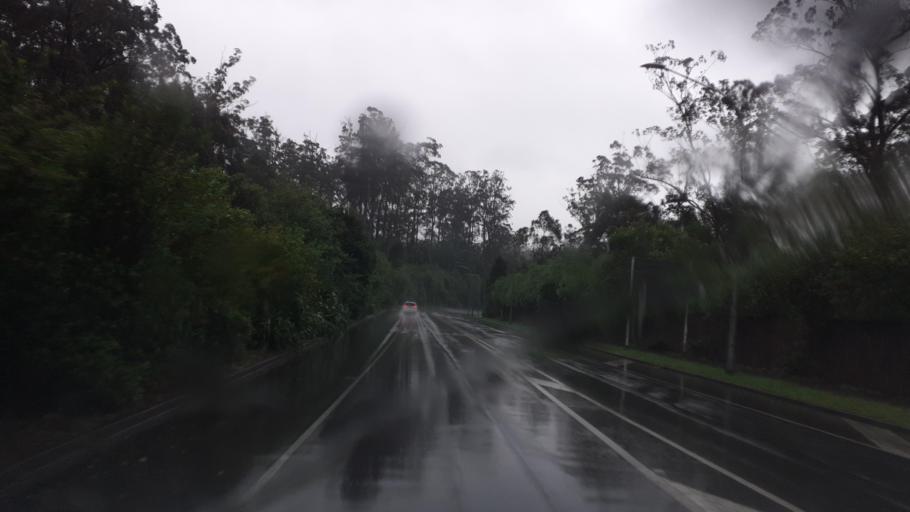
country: NZ
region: Northland
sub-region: Far North District
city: Kerikeri
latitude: -35.2211
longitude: 173.9527
